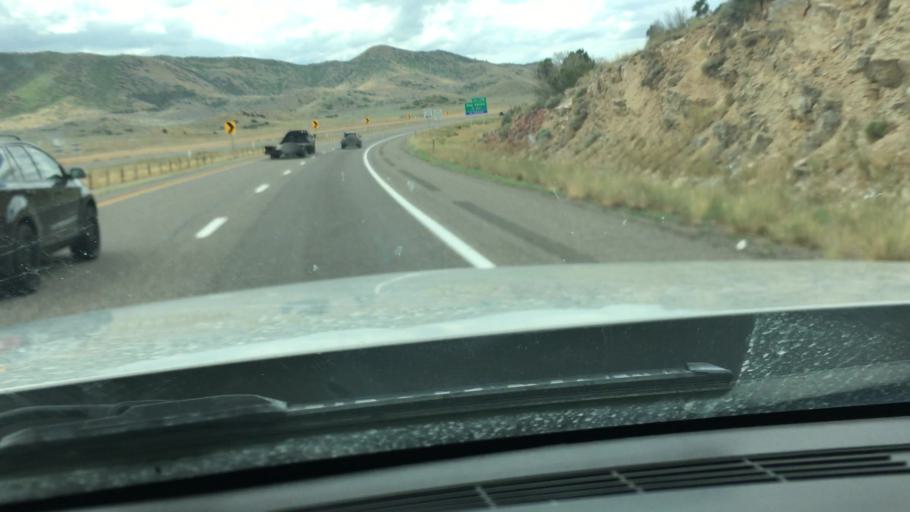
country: US
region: Utah
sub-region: Beaver County
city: Beaver
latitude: 38.6702
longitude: -112.5897
